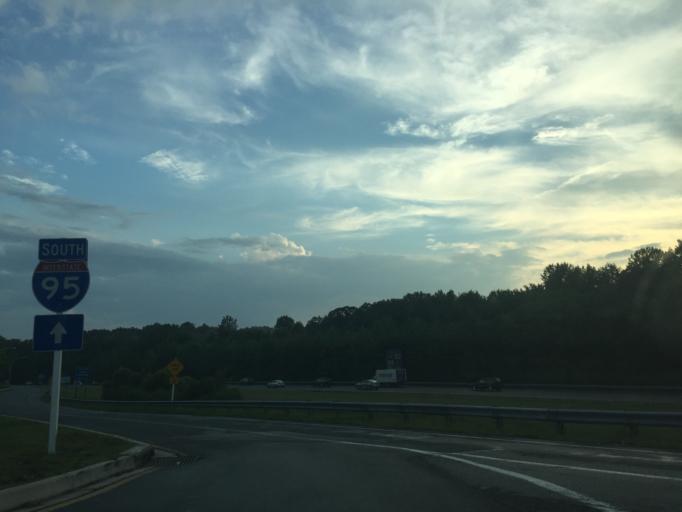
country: US
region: Maryland
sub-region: Harford County
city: Riverside
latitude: 39.4965
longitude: -76.2343
